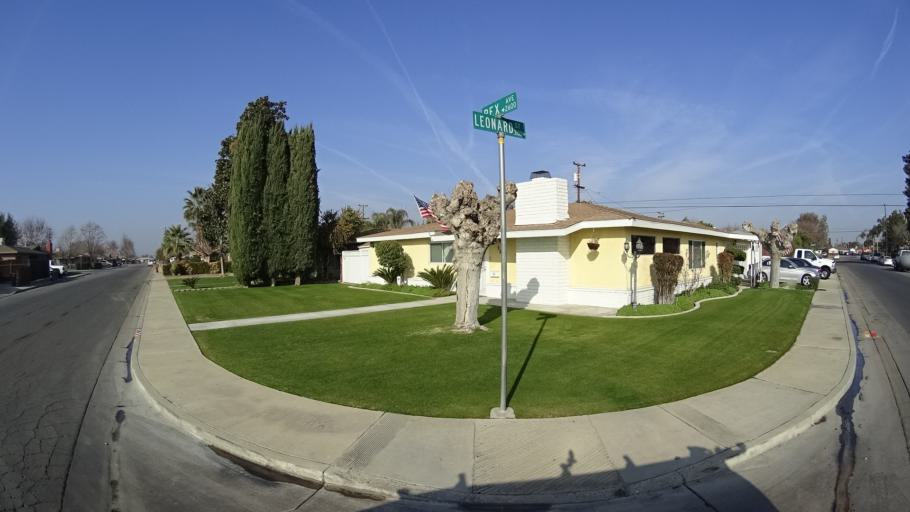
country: US
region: California
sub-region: Kern County
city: Bakersfield
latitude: 35.3264
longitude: -119.0312
